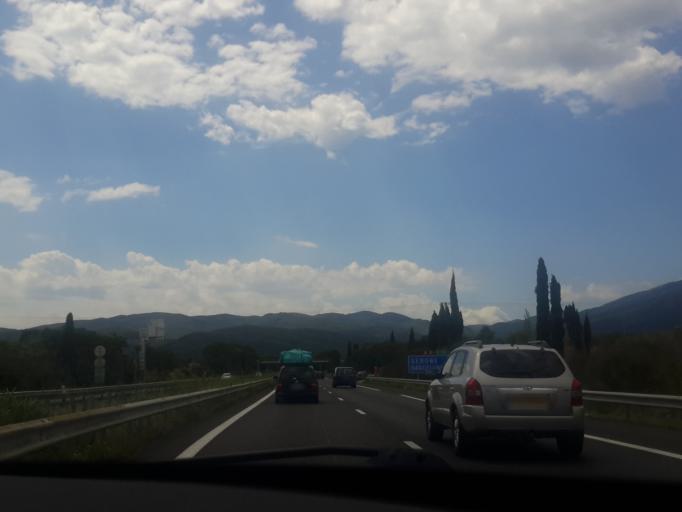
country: FR
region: Languedoc-Roussillon
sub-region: Departement des Pyrenees-Orientales
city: el Volo
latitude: 42.5136
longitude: 2.8185
